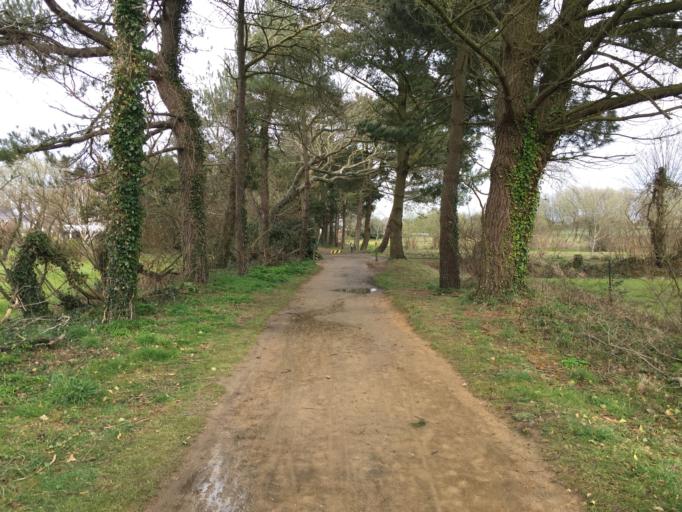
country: JE
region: St Helier
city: Saint Helier
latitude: 49.1824
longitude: -2.2258
